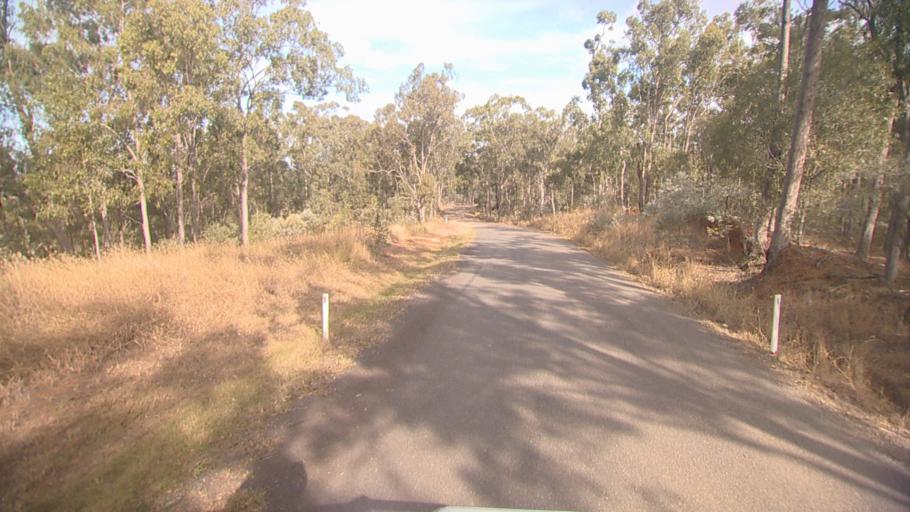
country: AU
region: Queensland
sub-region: Logan
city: Cedar Vale
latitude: -27.8973
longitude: 152.9882
